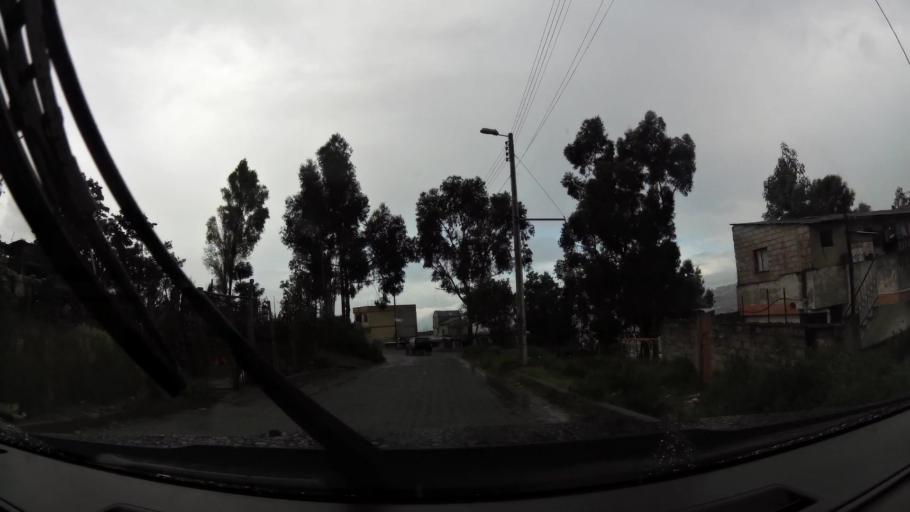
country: EC
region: Pichincha
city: Quito
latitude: -0.0982
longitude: -78.5137
